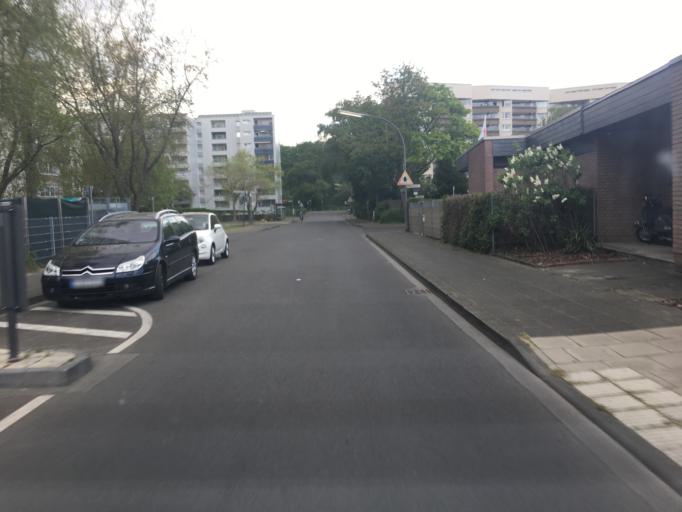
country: DE
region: North Rhine-Westphalia
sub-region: Regierungsbezirk Koln
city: Mengenich
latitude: 50.9824
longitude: 6.8653
